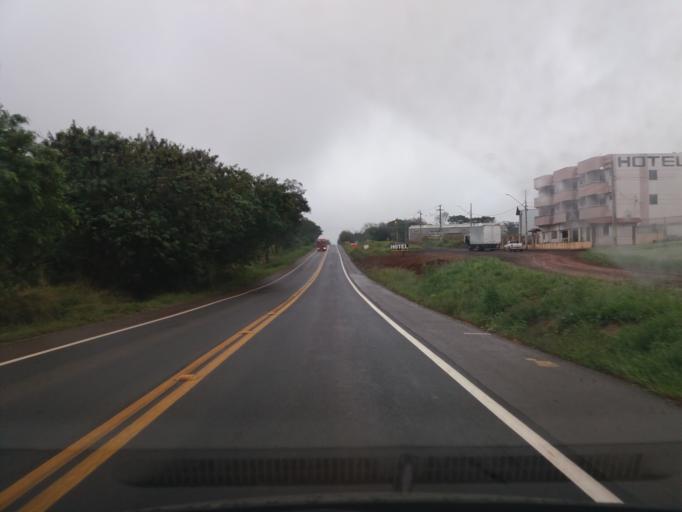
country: BR
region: Parana
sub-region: Realeza
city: Realeza
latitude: -25.5033
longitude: -53.5956
